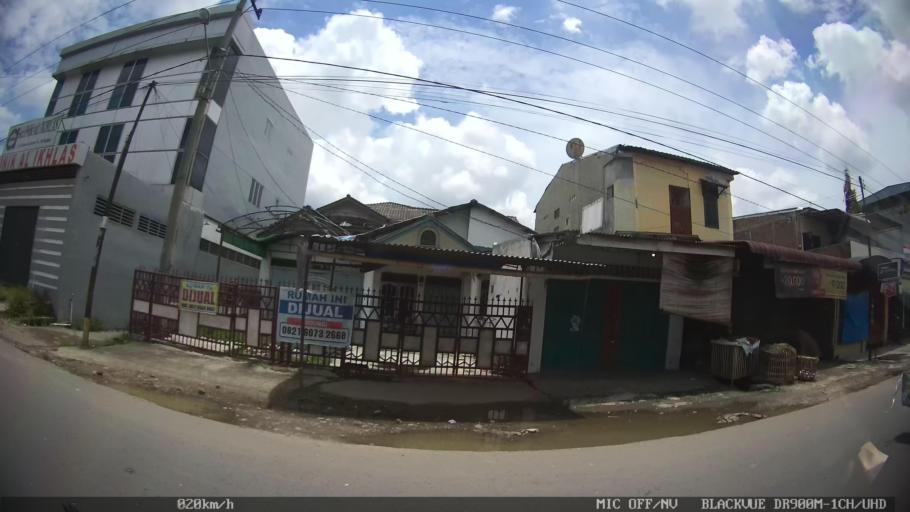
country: ID
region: North Sumatra
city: Medan
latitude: 3.5998
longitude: 98.7118
